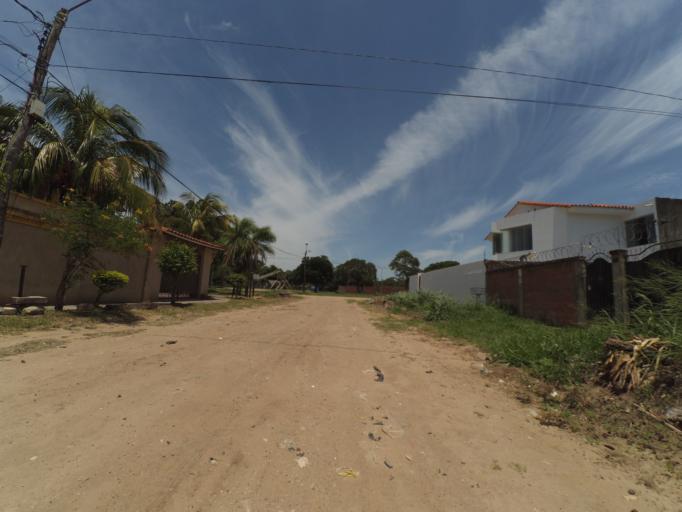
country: BO
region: Santa Cruz
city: Santa Cruz de la Sierra
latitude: -17.8124
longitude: -63.2259
